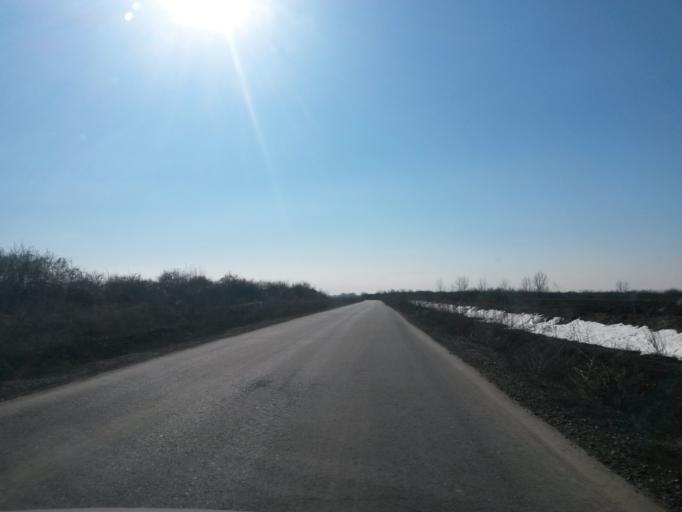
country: HR
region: Vukovarsko-Srijemska
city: Negoslavci
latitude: 45.3094
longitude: 19.0021
